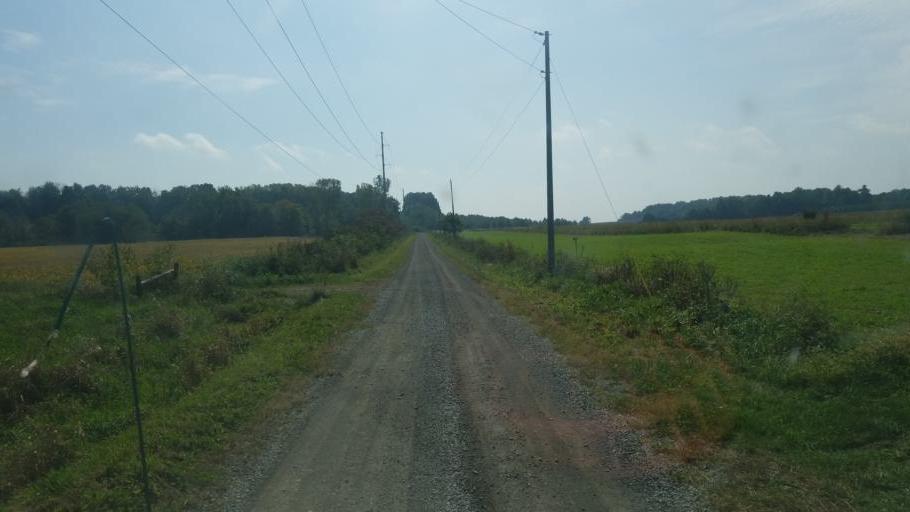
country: US
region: Ohio
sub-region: Knox County
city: Fredericktown
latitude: 40.5159
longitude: -82.4585
